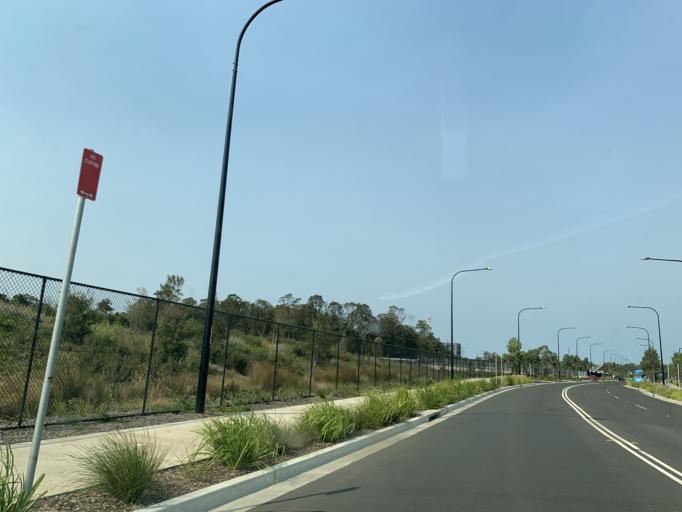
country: AU
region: New South Wales
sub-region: Blacktown
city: Rouse Hill
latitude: -33.6932
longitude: 150.9023
